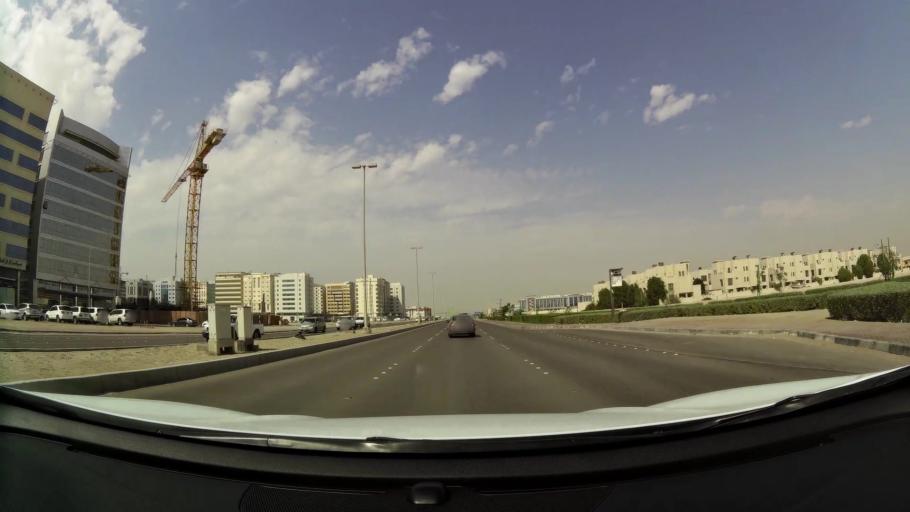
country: AE
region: Abu Dhabi
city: Abu Dhabi
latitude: 24.3410
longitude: 54.5383
